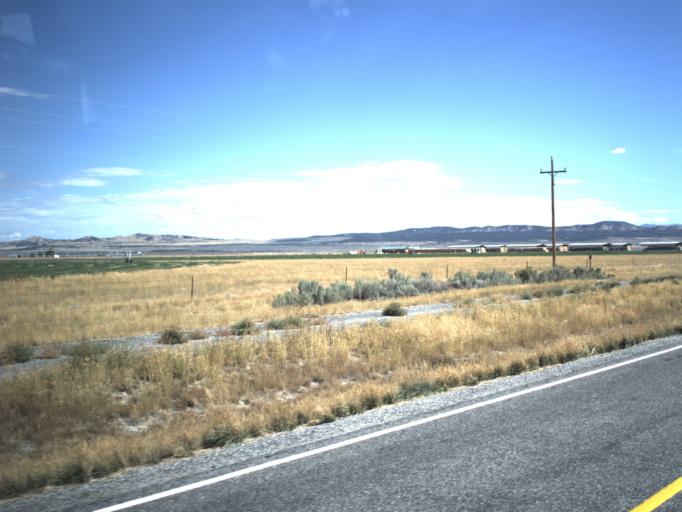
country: US
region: Idaho
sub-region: Oneida County
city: Malad City
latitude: 41.9665
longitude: -112.9141
